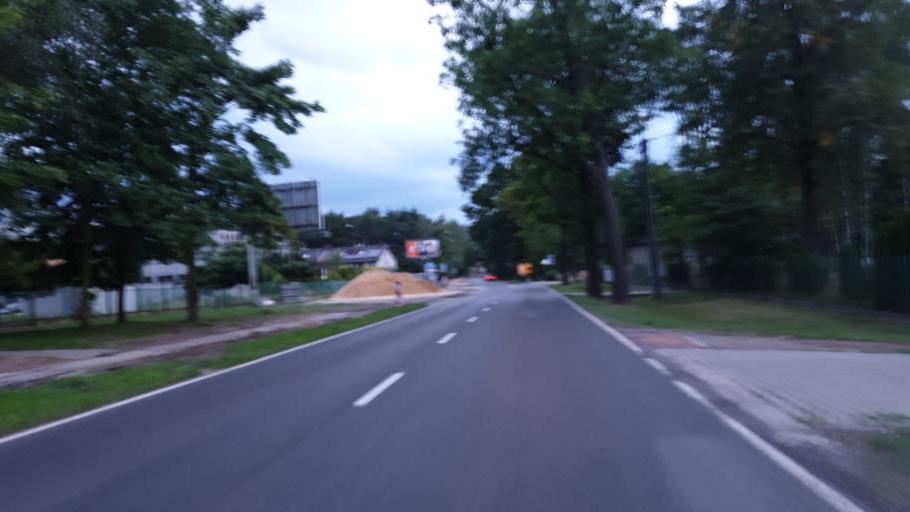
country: PL
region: Silesian Voivodeship
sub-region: Powiat mikolowski
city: Mikolow
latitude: 50.2292
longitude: 18.9339
